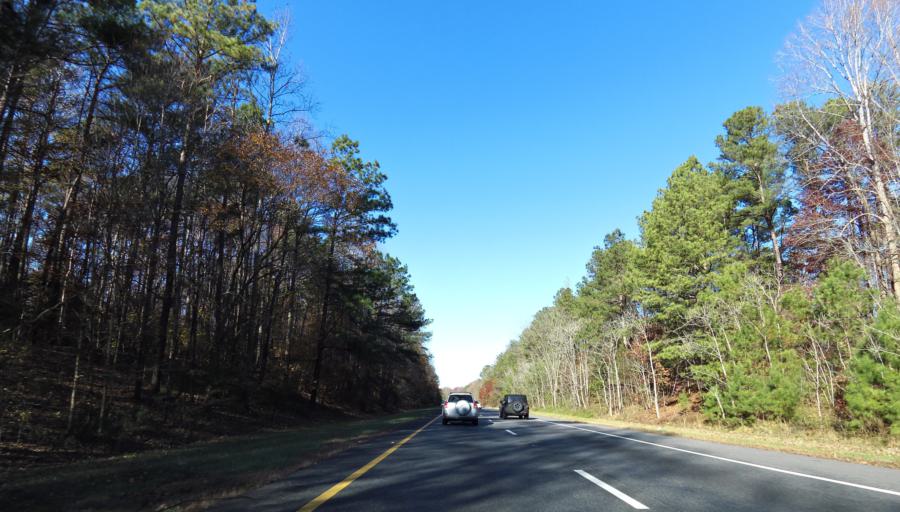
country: US
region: Virginia
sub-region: King William County
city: West Point
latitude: 37.4076
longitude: -76.7885
